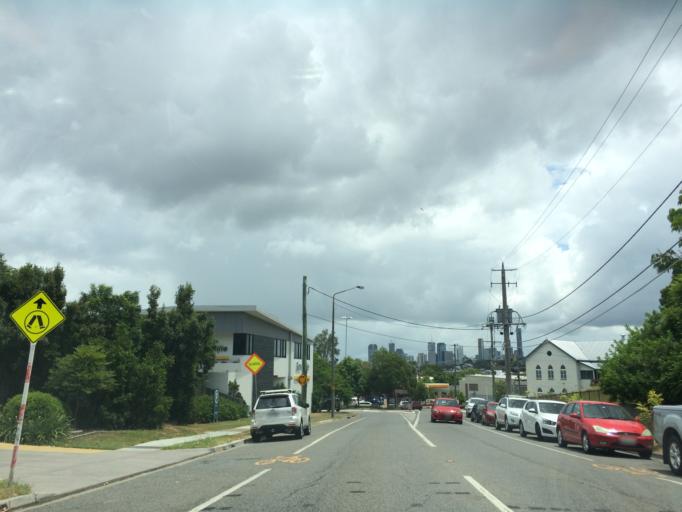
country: AU
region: Queensland
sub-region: Brisbane
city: Balmoral
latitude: -27.4511
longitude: 153.0633
